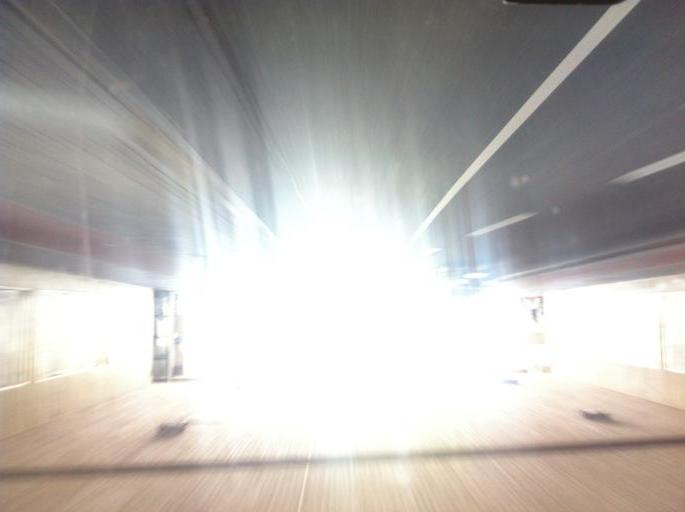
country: DE
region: North Rhine-Westphalia
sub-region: Regierungsbezirk Koln
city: Mengenich
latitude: 50.9487
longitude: 6.8880
